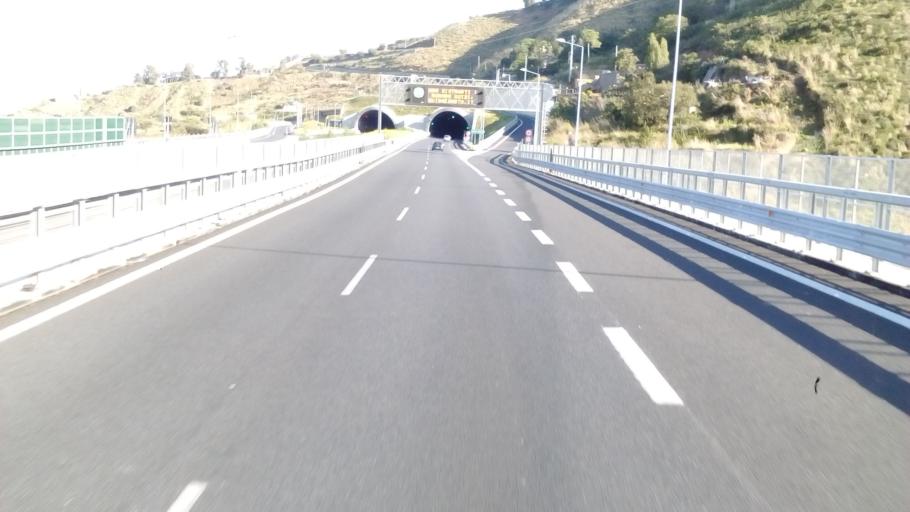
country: IT
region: Calabria
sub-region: Provincia di Reggio Calabria
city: Villa San Giovanni
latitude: 38.2384
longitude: 15.6798
